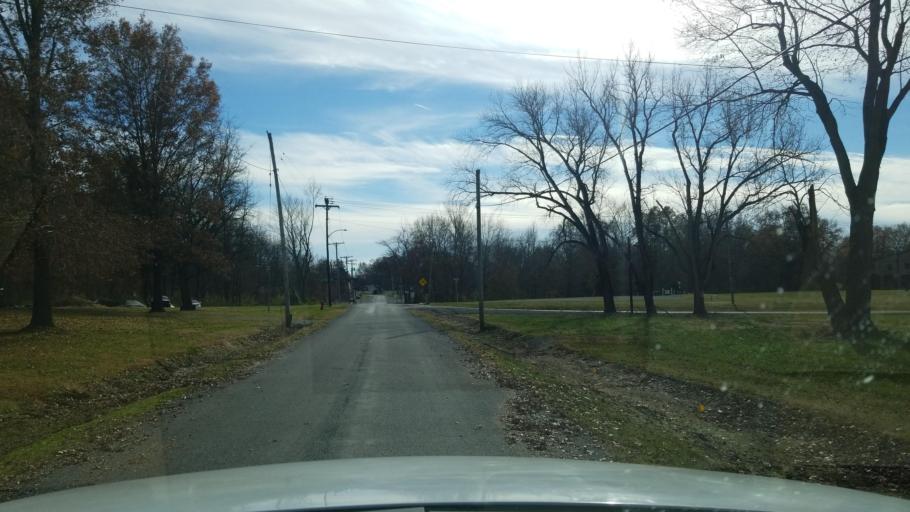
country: US
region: Illinois
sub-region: Saline County
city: Harrisburg
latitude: 37.7669
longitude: -88.5172
